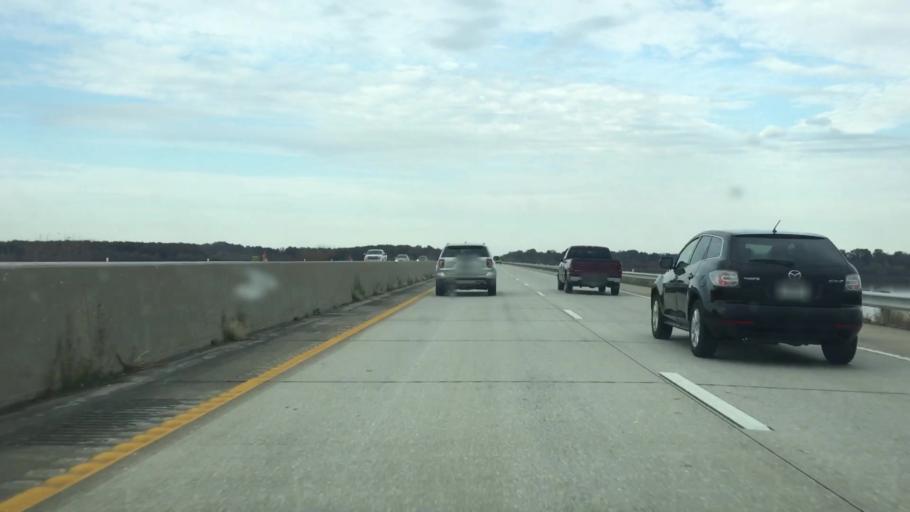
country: US
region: Missouri
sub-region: Henry County
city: Clinton
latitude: 38.2798
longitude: -93.7594
